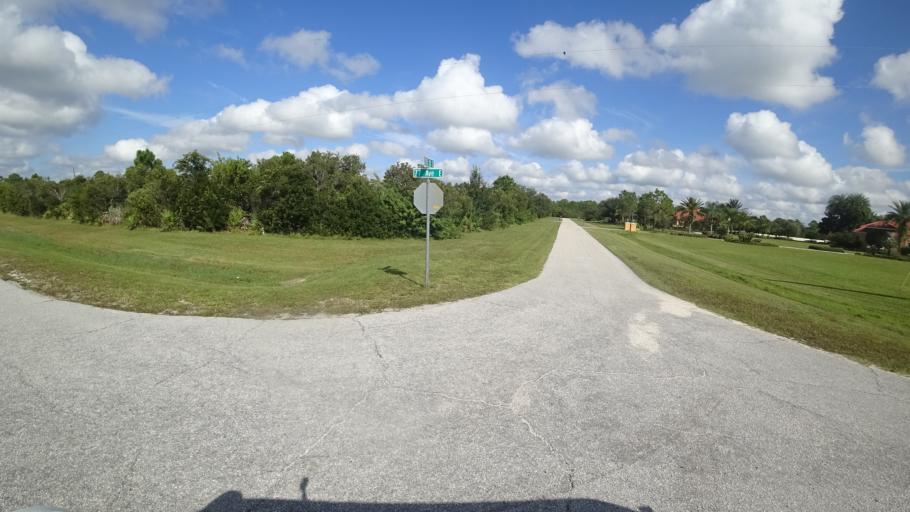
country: US
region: Florida
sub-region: Sarasota County
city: The Meadows
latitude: 27.4023
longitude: -82.3326
